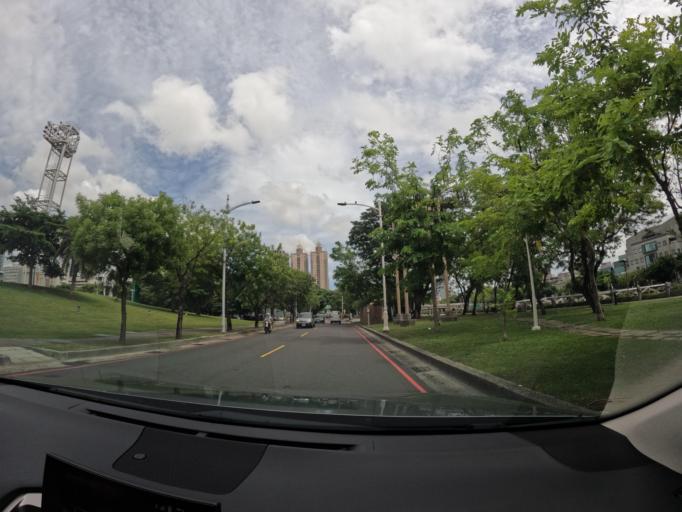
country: TW
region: Kaohsiung
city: Kaohsiung
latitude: 22.6292
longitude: 120.2877
